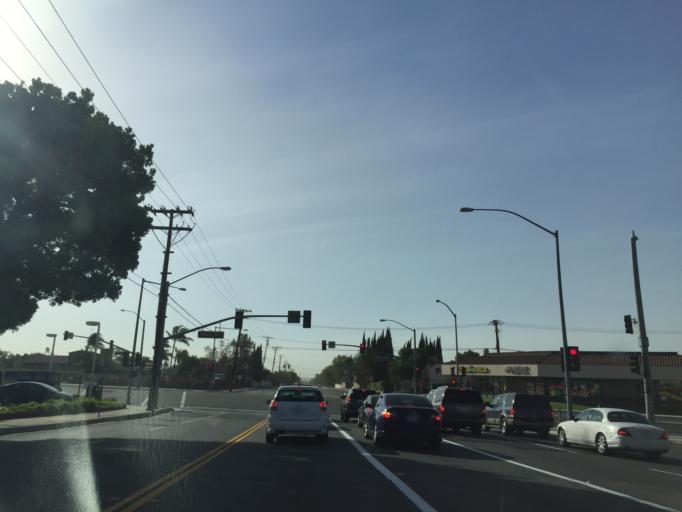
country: US
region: California
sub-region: Orange County
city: Yorba Linda
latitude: 33.9049
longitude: -117.8422
